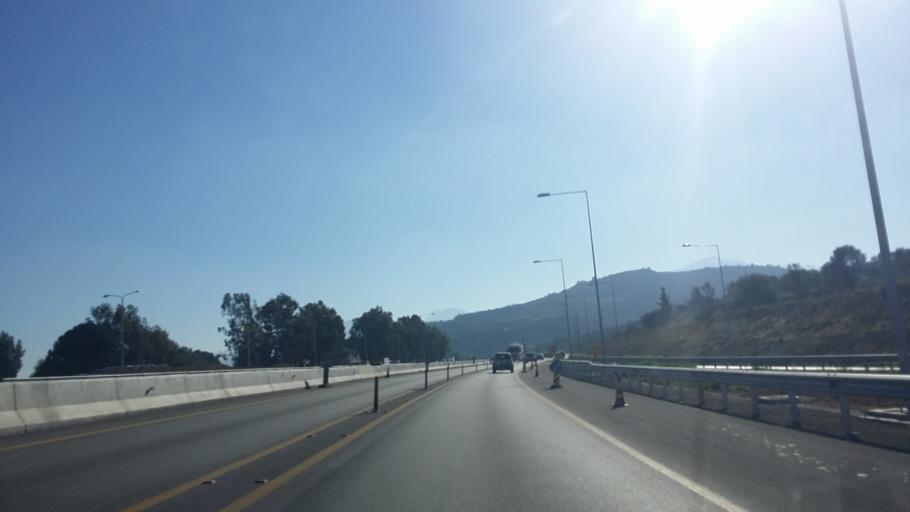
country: GR
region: West Greece
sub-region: Nomos Achaias
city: Selianitika
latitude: 38.2853
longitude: 22.0219
